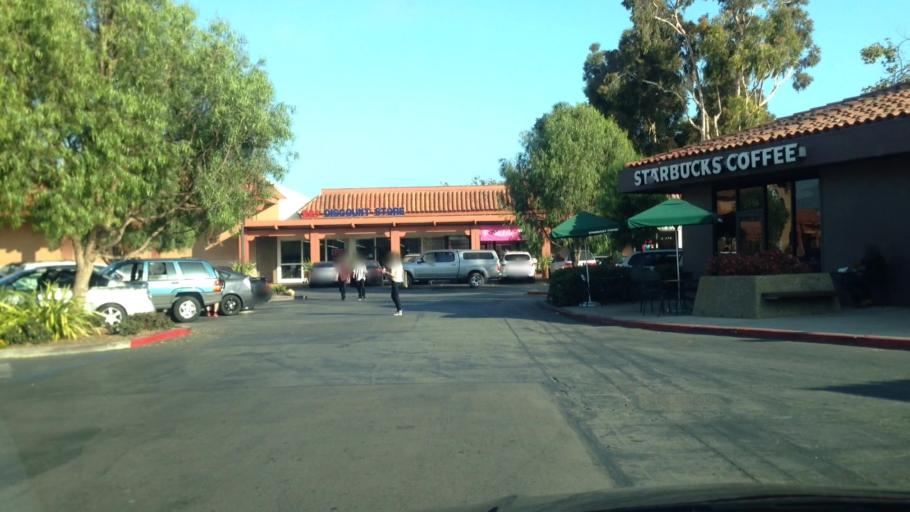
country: US
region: California
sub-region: Santa Barbara County
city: Carpinteria
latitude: 34.3952
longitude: -119.5132
